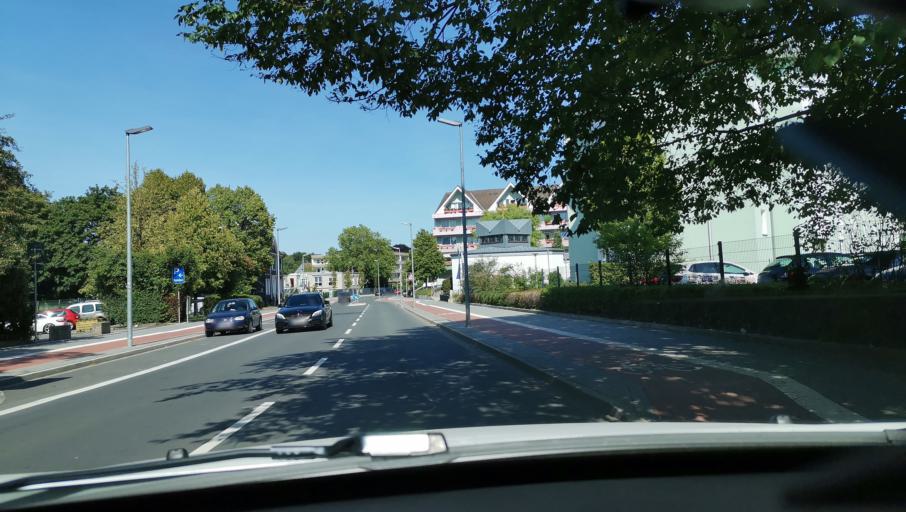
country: DE
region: North Rhine-Westphalia
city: Ennepetal
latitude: 51.3343
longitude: 7.3786
